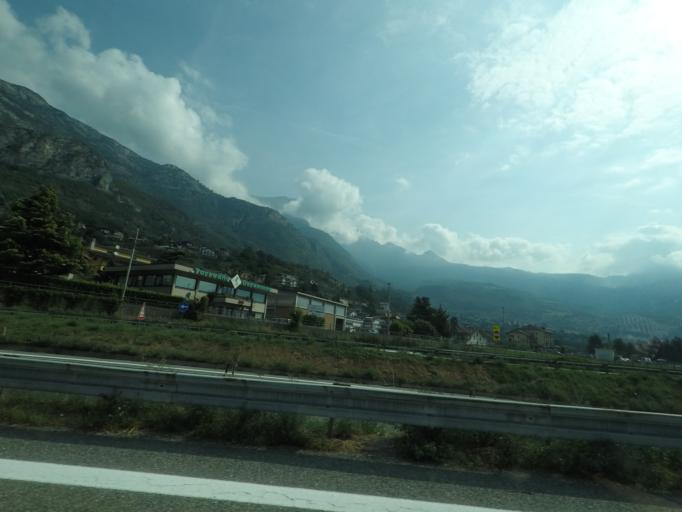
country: IT
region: Aosta Valley
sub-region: Valle d'Aosta
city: Chatillon
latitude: 45.7489
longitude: 7.6212
